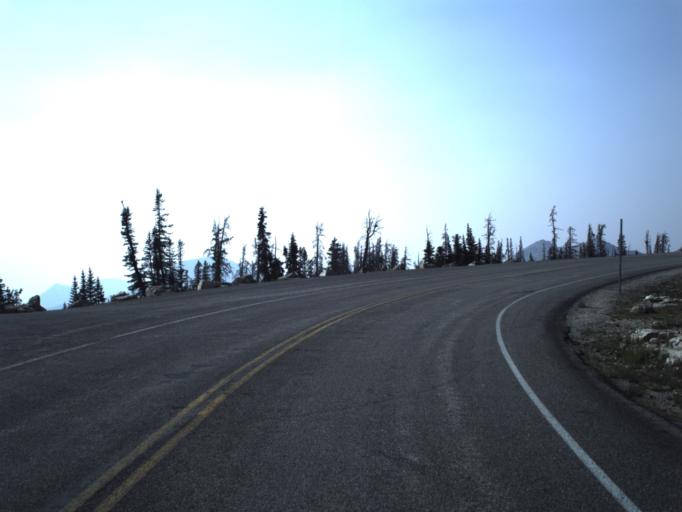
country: US
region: Utah
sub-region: Summit County
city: Kamas
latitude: 40.6863
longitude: -110.9061
